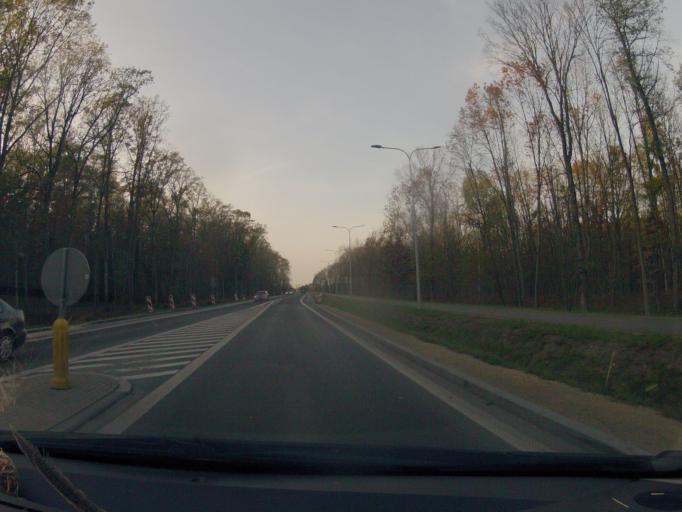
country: PL
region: Opole Voivodeship
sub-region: Powiat opolski
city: Tarnow Opolski
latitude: 50.5968
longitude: 18.0900
